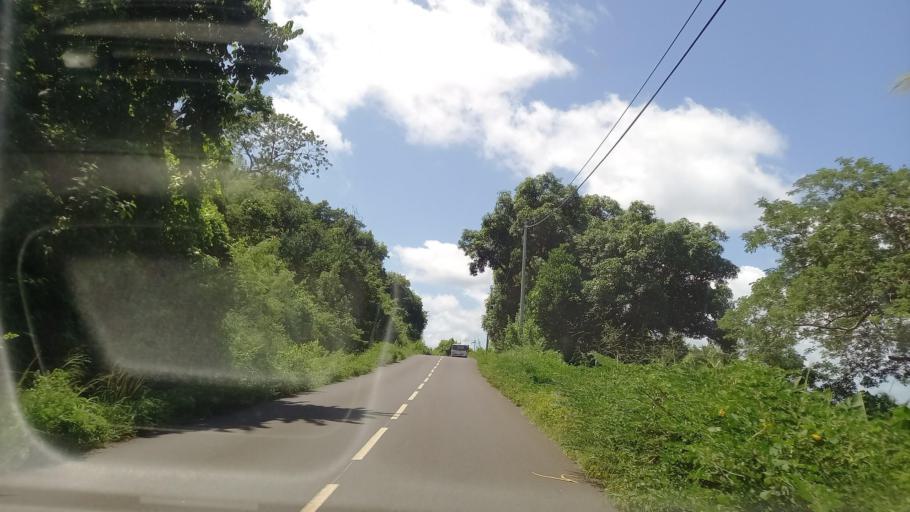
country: YT
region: Bandraboua
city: Bandraboua
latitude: -12.6860
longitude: 45.1051
